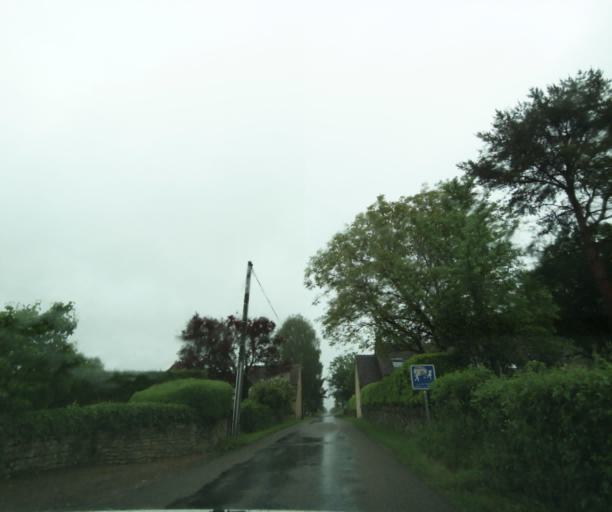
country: FR
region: Bourgogne
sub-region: Departement de Saone-et-Loire
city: Charolles
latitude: 46.4114
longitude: 4.2604
